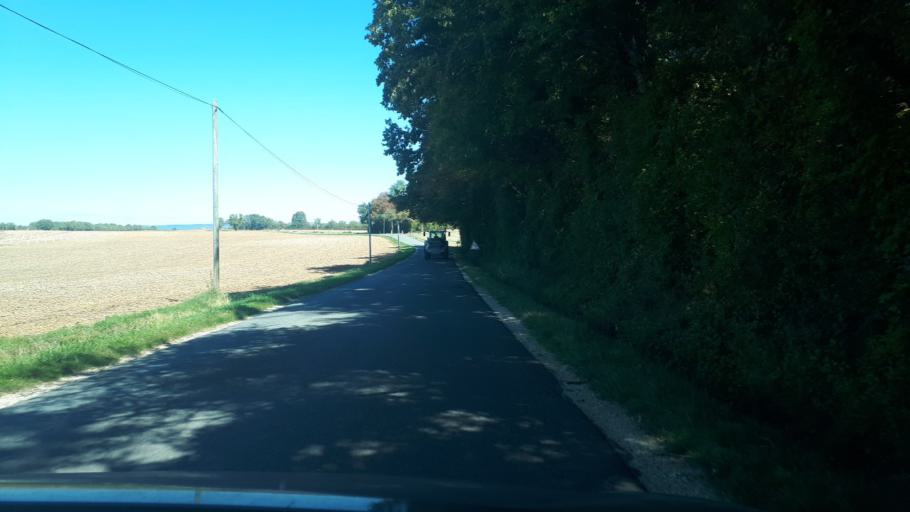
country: FR
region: Centre
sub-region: Departement du Cher
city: Sainte-Solange
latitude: 47.1499
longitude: 2.5617
